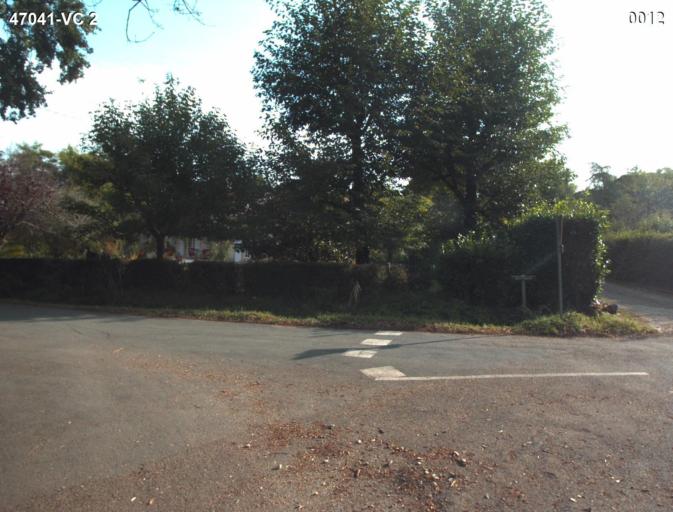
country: FR
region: Aquitaine
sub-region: Departement du Lot-et-Garonne
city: Port-Sainte-Marie
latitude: 44.2008
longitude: 0.4139
